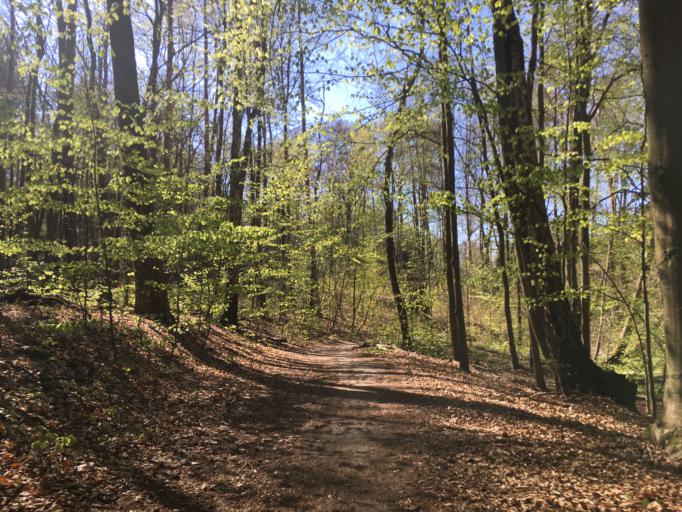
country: DE
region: Brandenburg
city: Wandlitz
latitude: 52.7485
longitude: 13.4962
